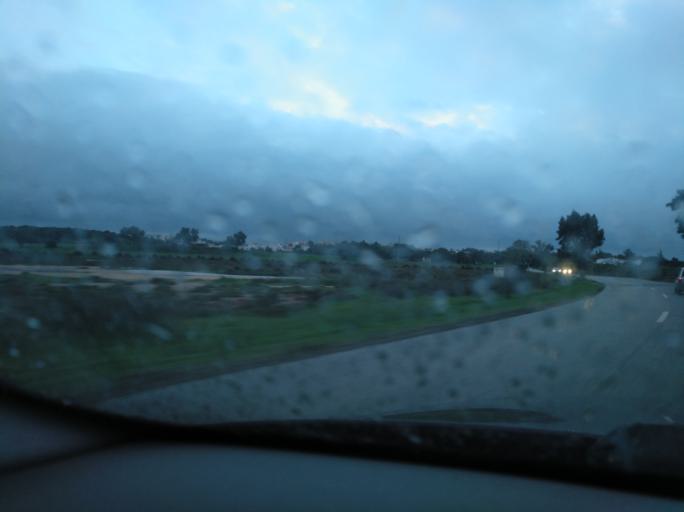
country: PT
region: Faro
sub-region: Vila Real de Santo Antonio
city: Monte Gordo
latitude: 37.2014
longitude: -7.4802
